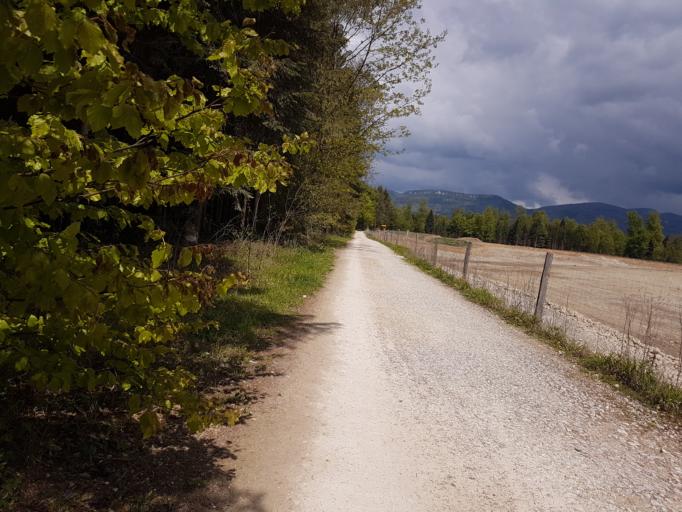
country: CH
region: Aargau
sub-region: Bezirk Zofingen
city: Fulenbach
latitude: 47.2928
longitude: 7.8433
